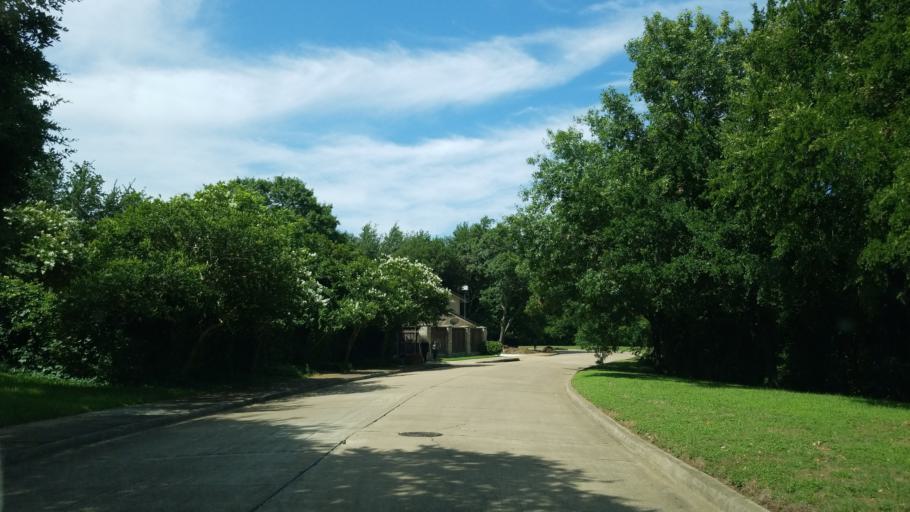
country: US
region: Texas
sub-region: Dallas County
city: Farmers Branch
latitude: 32.9061
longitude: -96.8463
